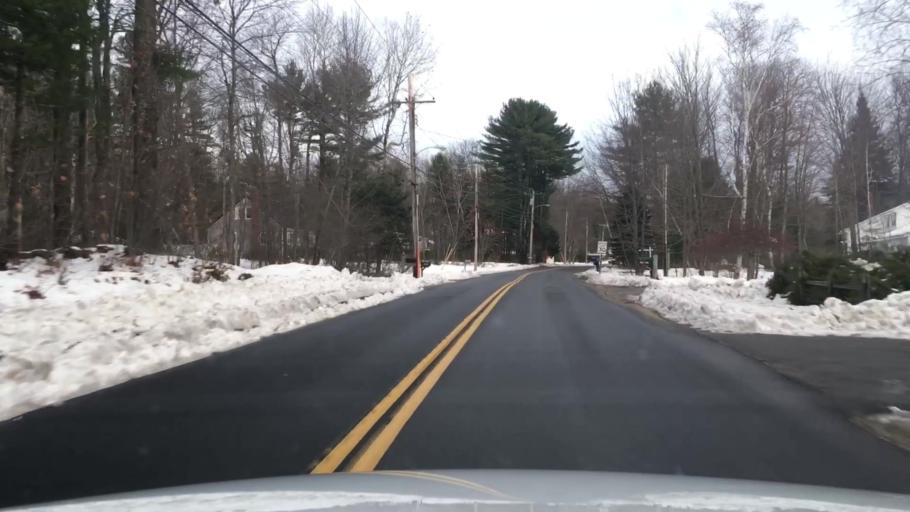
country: US
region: Maine
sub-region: Cumberland County
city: Yarmouth
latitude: 43.7895
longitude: -70.1980
